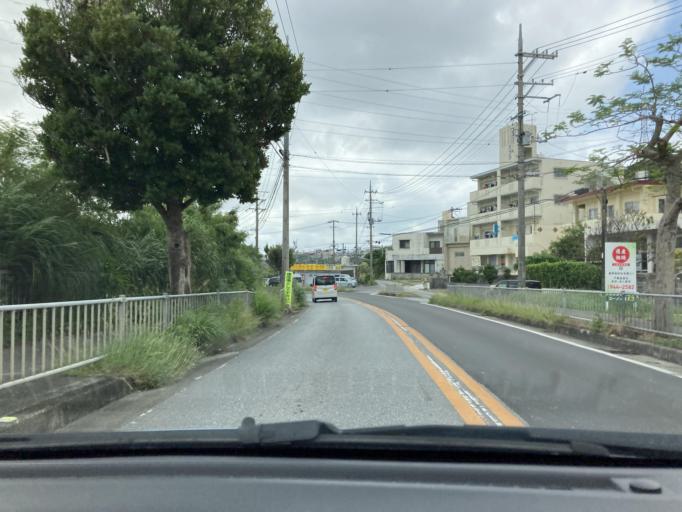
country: JP
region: Okinawa
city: Ginowan
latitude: 26.2406
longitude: 127.7502
